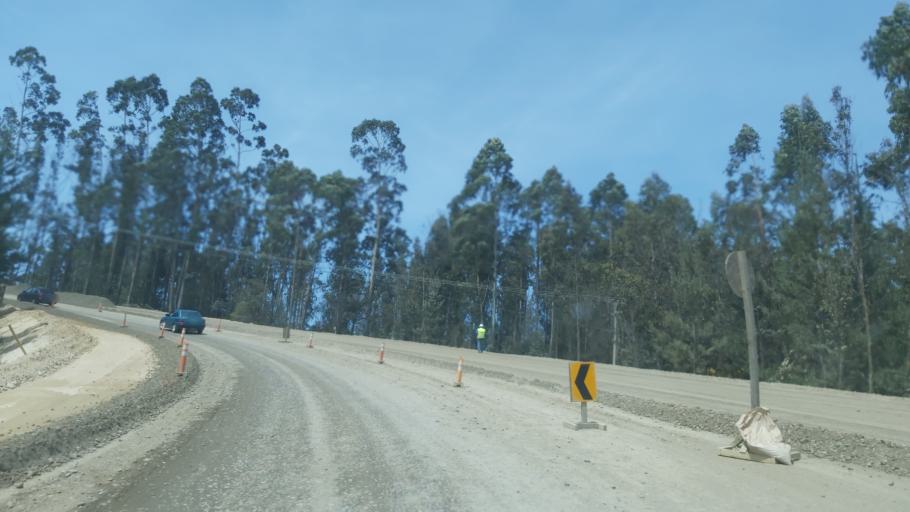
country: CL
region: Maule
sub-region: Provincia de Talca
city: Constitucion
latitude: -35.3869
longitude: -72.4207
